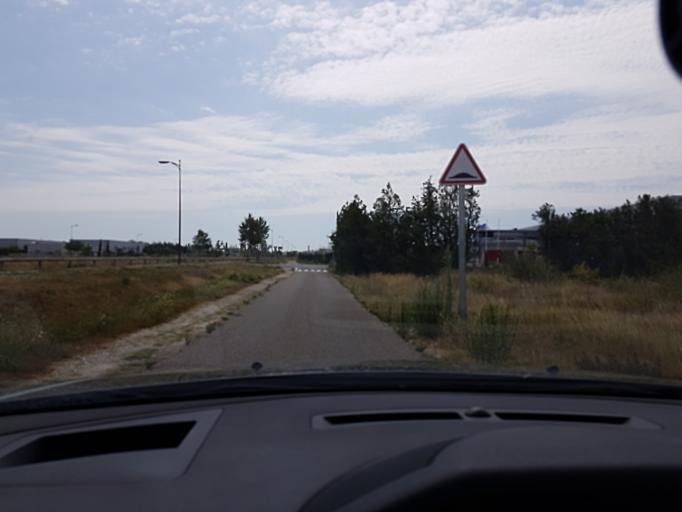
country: FR
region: Provence-Alpes-Cote d'Azur
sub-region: Departement du Vaucluse
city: Entraigues-sur-la-Sorgue
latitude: 43.9887
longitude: 4.9264
